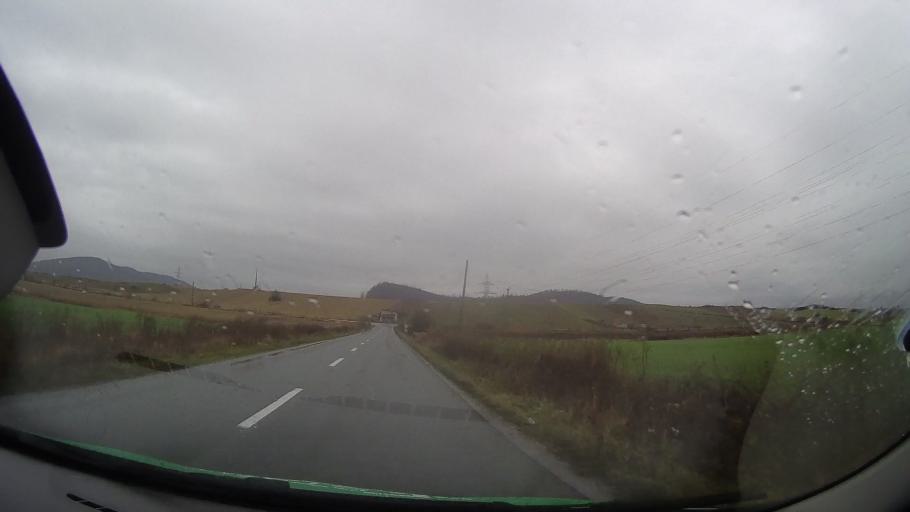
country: RO
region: Bistrita-Nasaud
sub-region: Municipiul Bistrita
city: Viisoara
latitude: 47.0549
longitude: 24.4501
